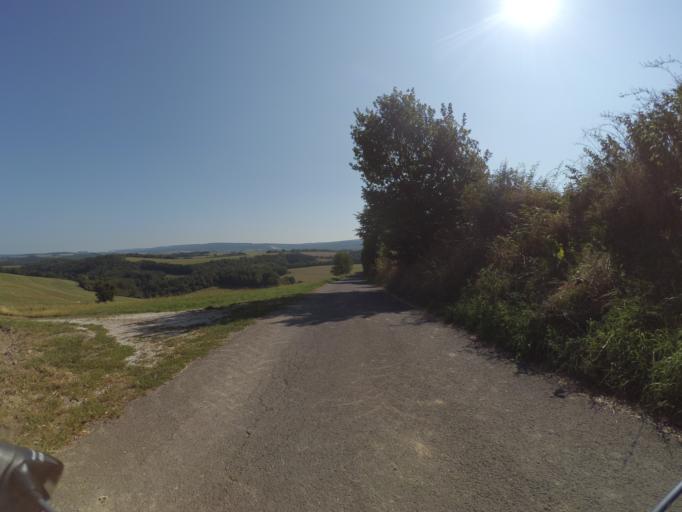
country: DE
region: Rheinland-Pfalz
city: Immert
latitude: 49.7632
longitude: 7.0273
